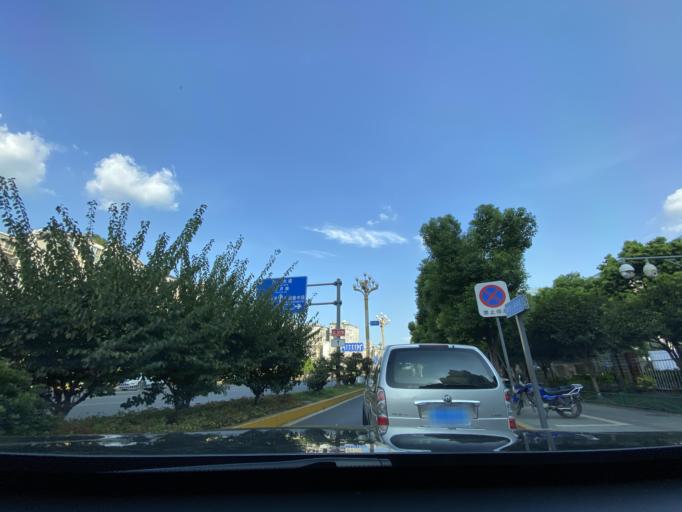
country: CN
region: Sichuan
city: Jiancheng
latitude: 30.4117
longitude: 104.5367
